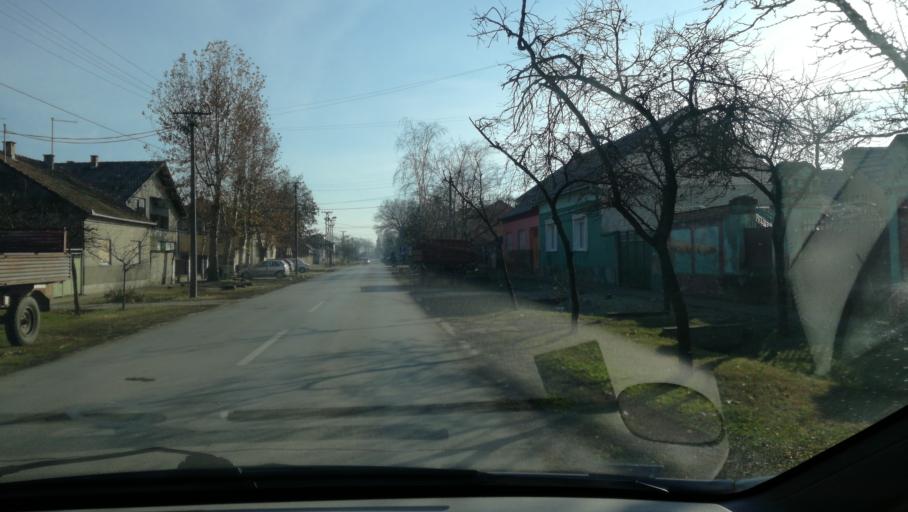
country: RS
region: Autonomna Pokrajina Vojvodina
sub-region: Severnobanatski Okrug
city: Kikinda
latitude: 45.8230
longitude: 20.4645
